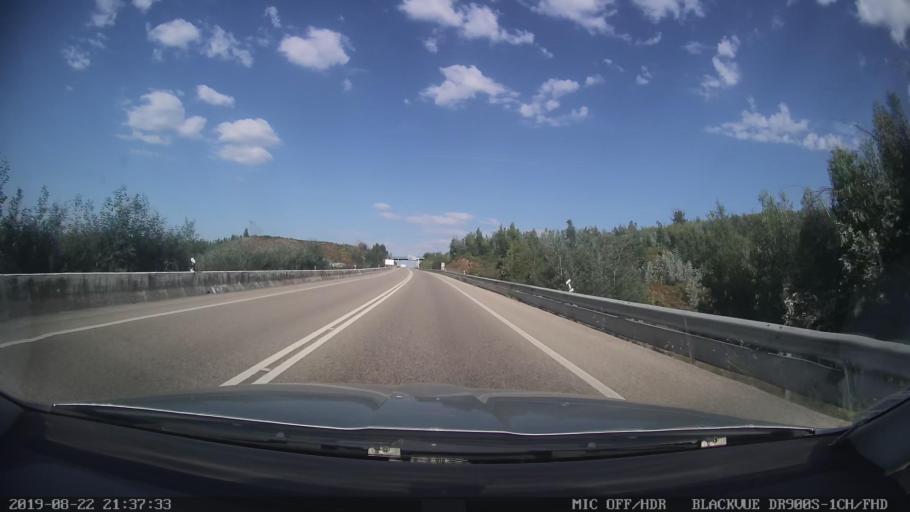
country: PT
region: Leiria
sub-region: Figueiro Dos Vinhos
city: Figueiro dos Vinhos
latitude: 39.9321
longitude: -8.2497
